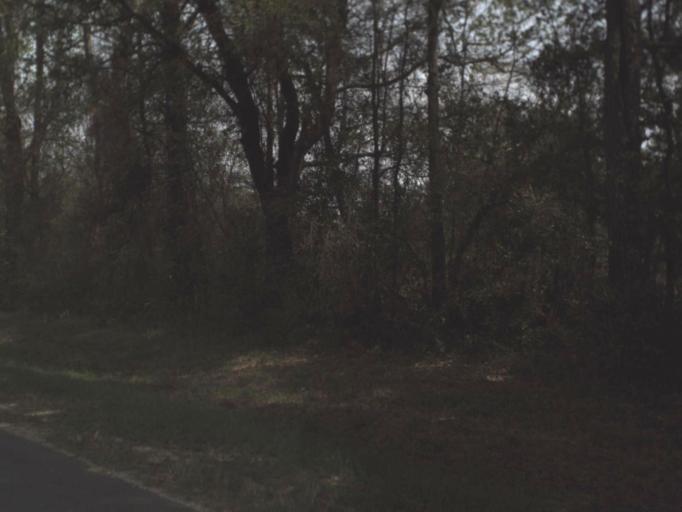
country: US
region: Florida
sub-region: Jackson County
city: Graceville
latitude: 30.9279
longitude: -85.4242
